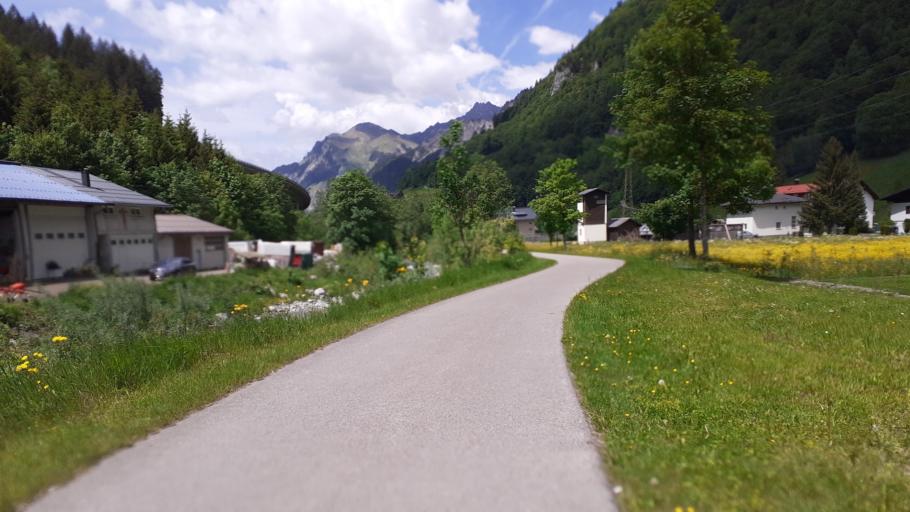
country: AT
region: Vorarlberg
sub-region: Politischer Bezirk Bludenz
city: Klosterle
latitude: 47.1303
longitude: 10.0854
